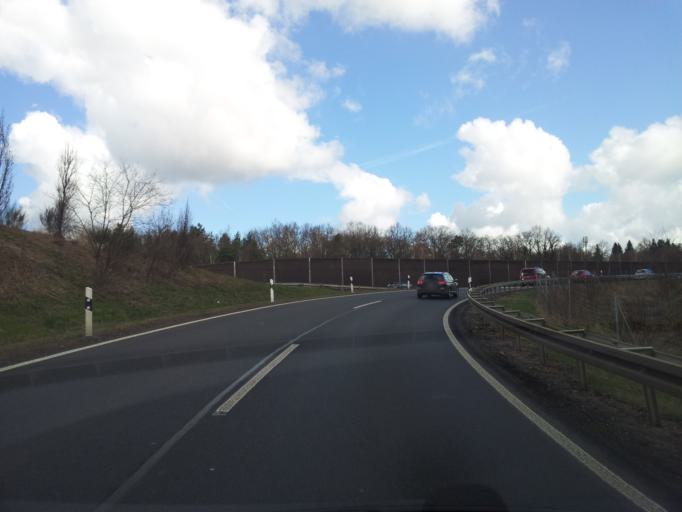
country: DE
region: Saxony
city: Albertstadt
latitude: 51.1078
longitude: 13.7362
